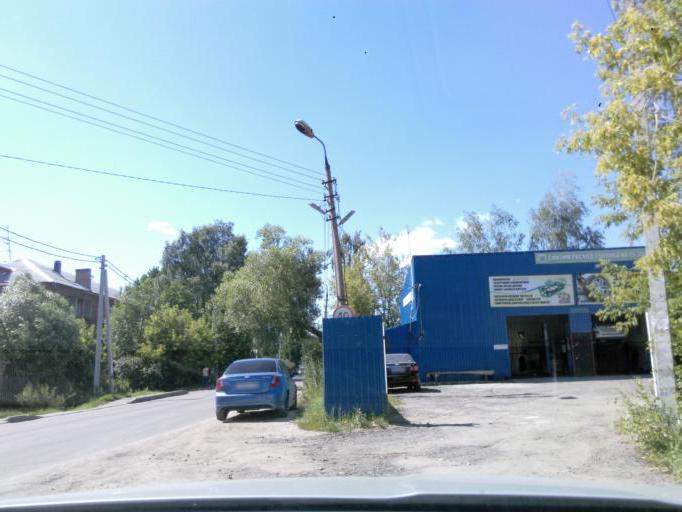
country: RU
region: Moskovskaya
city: Solnechnogorsk
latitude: 56.1810
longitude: 36.9761
